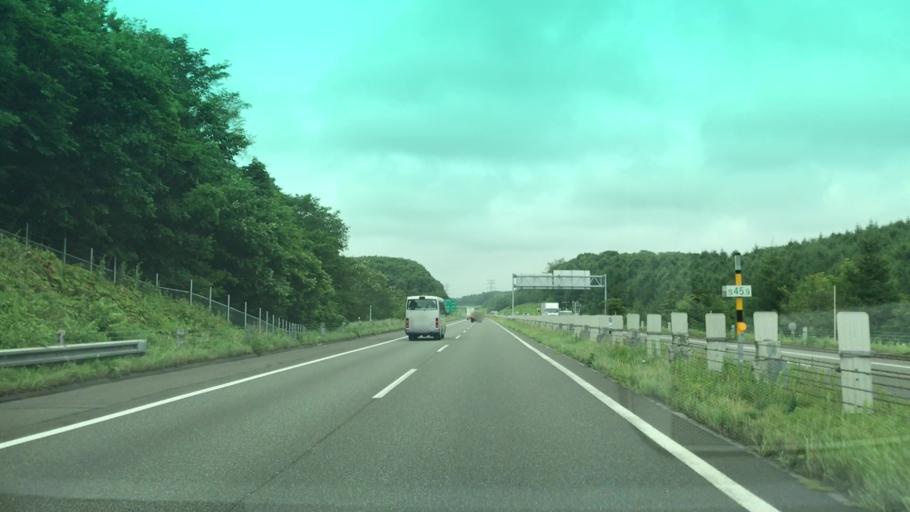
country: JP
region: Hokkaido
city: Tomakomai
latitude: 42.7214
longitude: 141.6527
